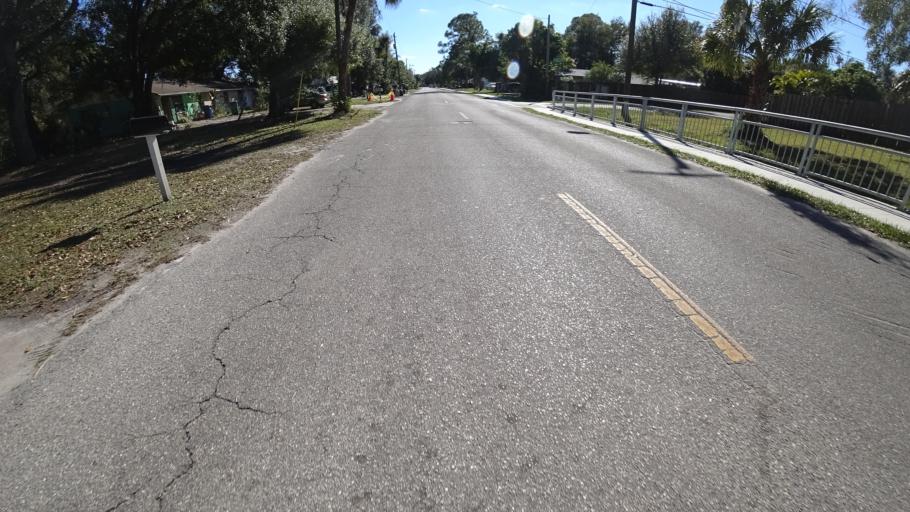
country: US
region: Florida
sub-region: Manatee County
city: Whitfield
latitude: 27.4318
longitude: -82.5508
